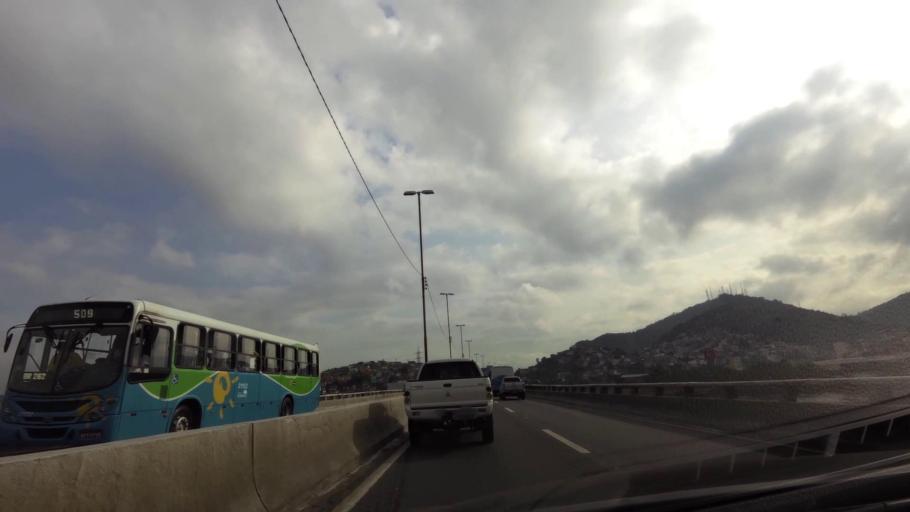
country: BR
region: Espirito Santo
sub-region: Vitoria
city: Vitoria
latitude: -20.3249
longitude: -40.3546
